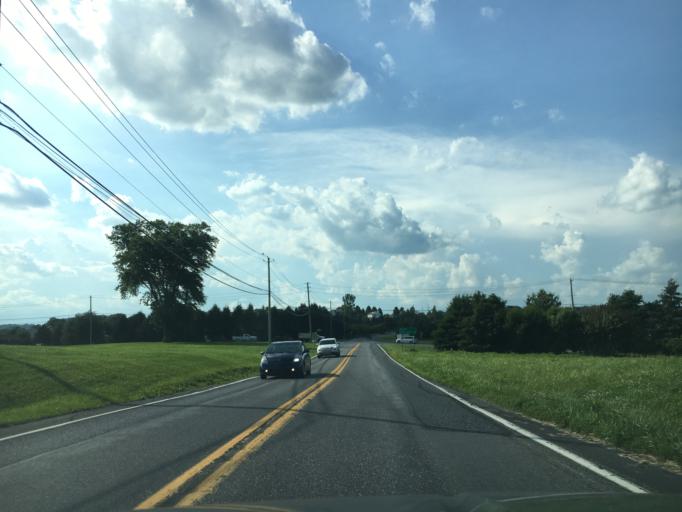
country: US
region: Pennsylvania
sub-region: Lehigh County
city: Schnecksville
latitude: 40.6944
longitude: -75.5918
